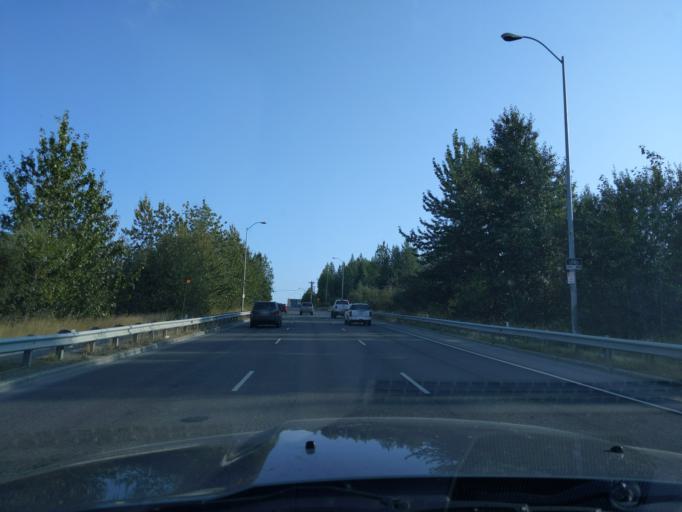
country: US
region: Alaska
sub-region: Anchorage Municipality
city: Anchorage
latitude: 61.2027
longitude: -149.8875
